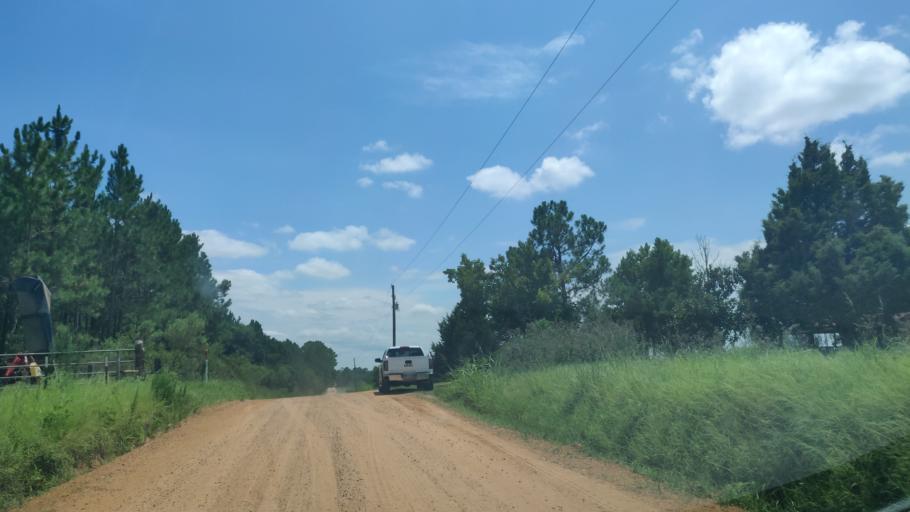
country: US
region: Georgia
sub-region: Tift County
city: Tifton
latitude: 31.4680
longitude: -83.6374
